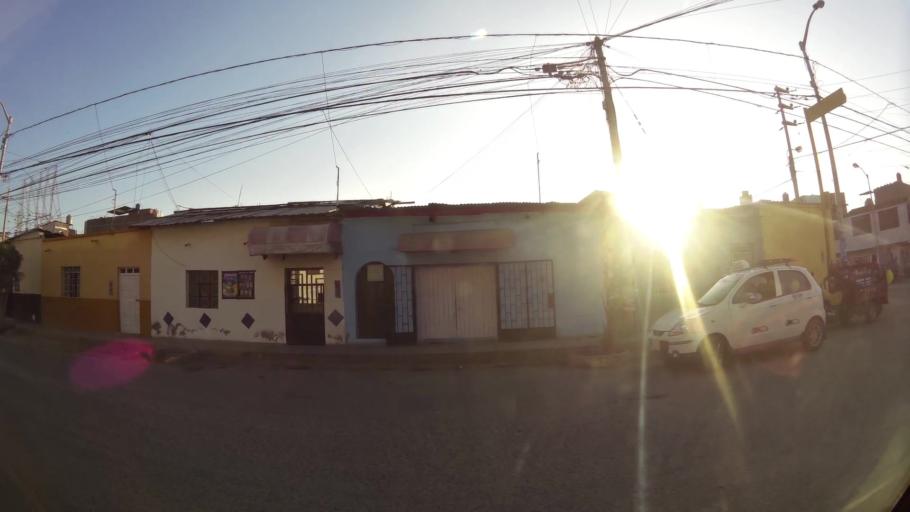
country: PE
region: Lambayeque
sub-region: Provincia de Chiclayo
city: Chiclayo
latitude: -6.7754
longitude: -79.8341
